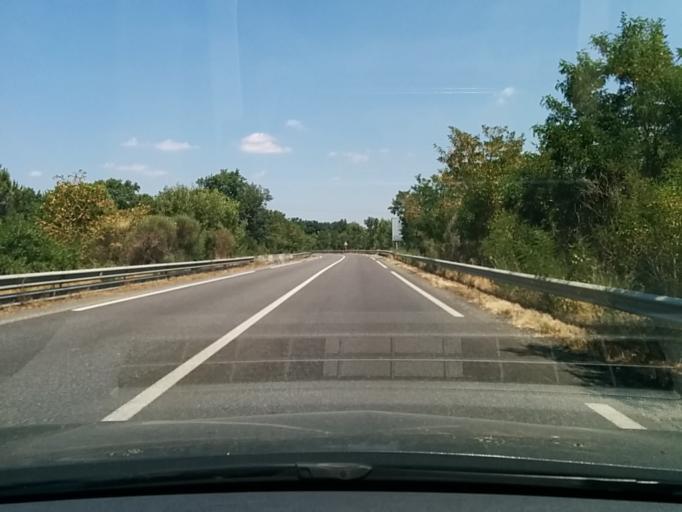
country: FR
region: Midi-Pyrenees
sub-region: Departement de la Haute-Garonne
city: Labege
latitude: 43.5277
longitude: 1.5213
